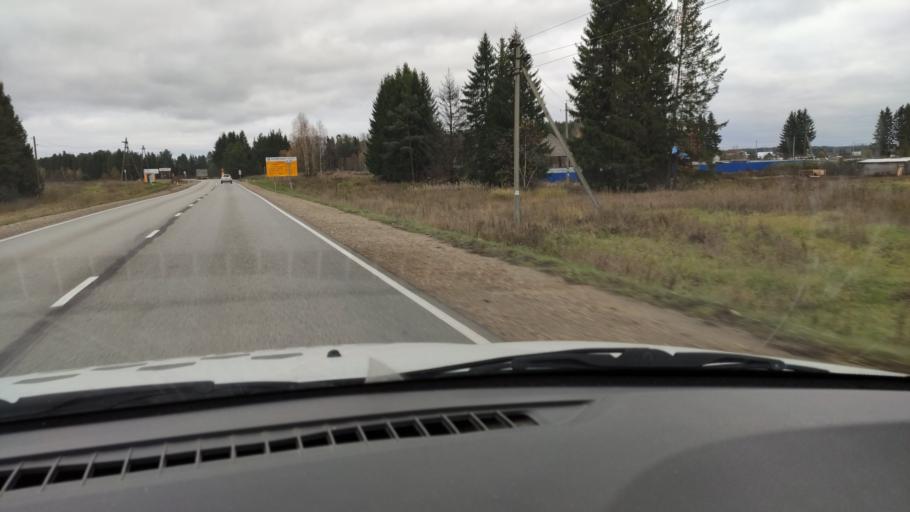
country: RU
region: Kirov
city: Slobodskoy
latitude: 58.7808
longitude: 50.4378
